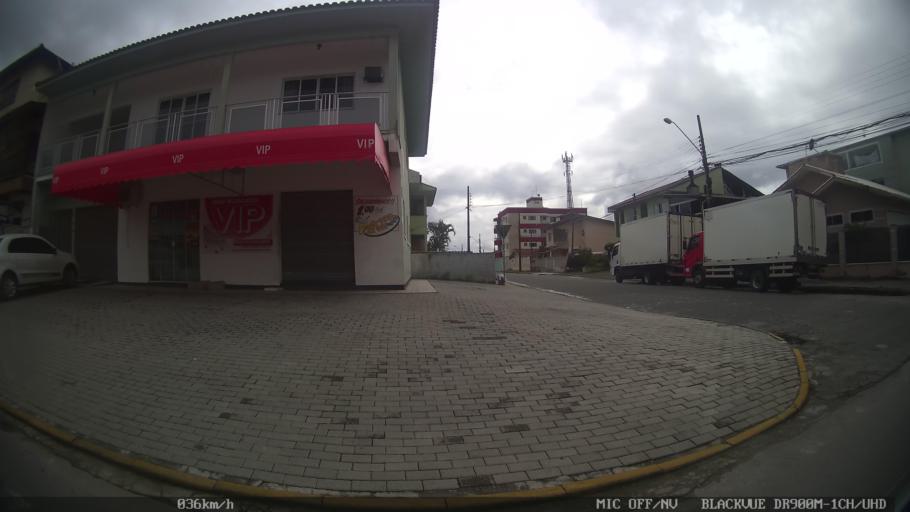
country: BR
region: Santa Catarina
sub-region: Biguacu
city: Biguacu
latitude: -27.5098
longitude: -48.6540
